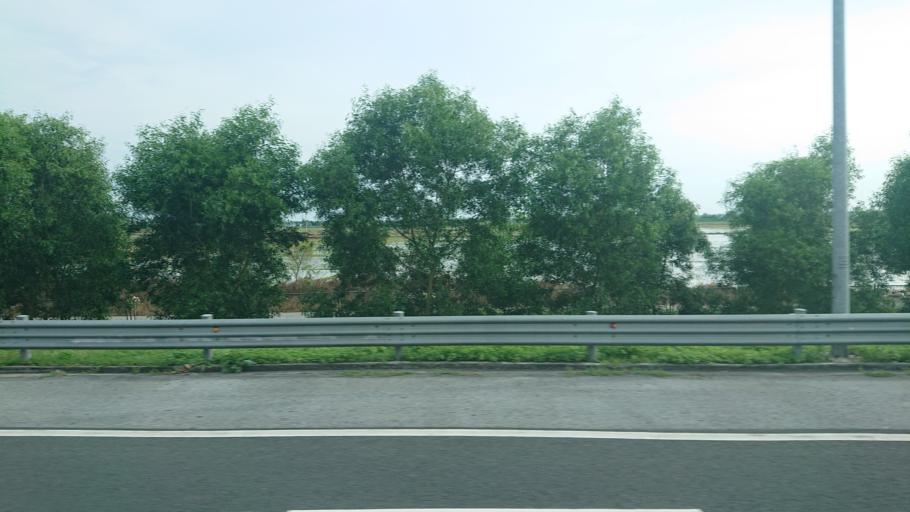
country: VN
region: Hai Phong
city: An Lao
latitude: 20.7956
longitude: 106.5443
